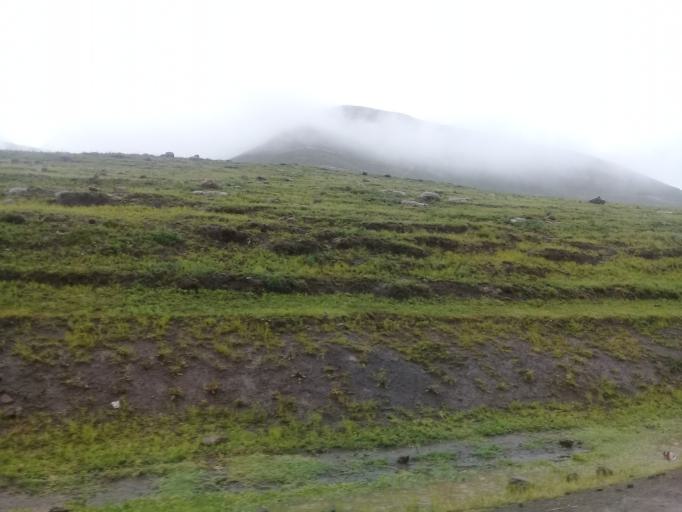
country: LS
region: Mokhotlong
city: Mokhotlong
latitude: -29.3872
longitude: 28.9524
